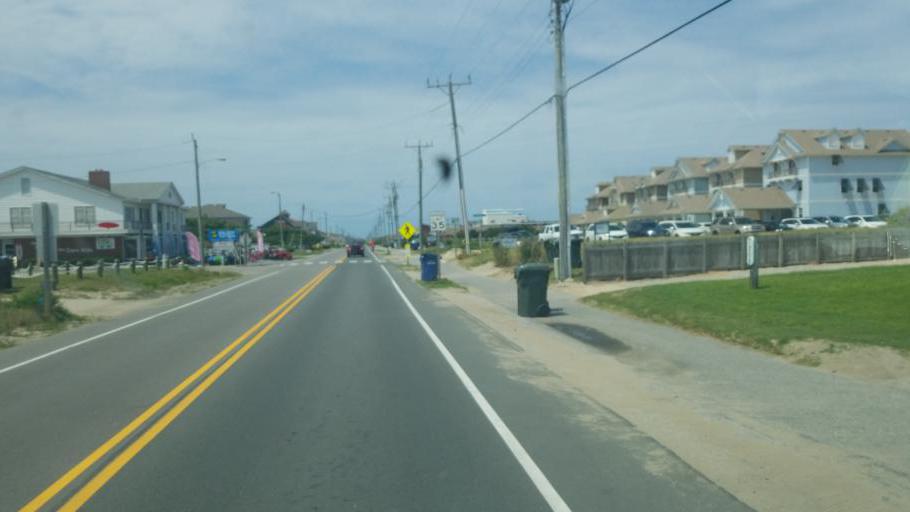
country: US
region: North Carolina
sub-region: Dare County
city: Nags Head
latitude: 35.9105
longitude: -75.5978
